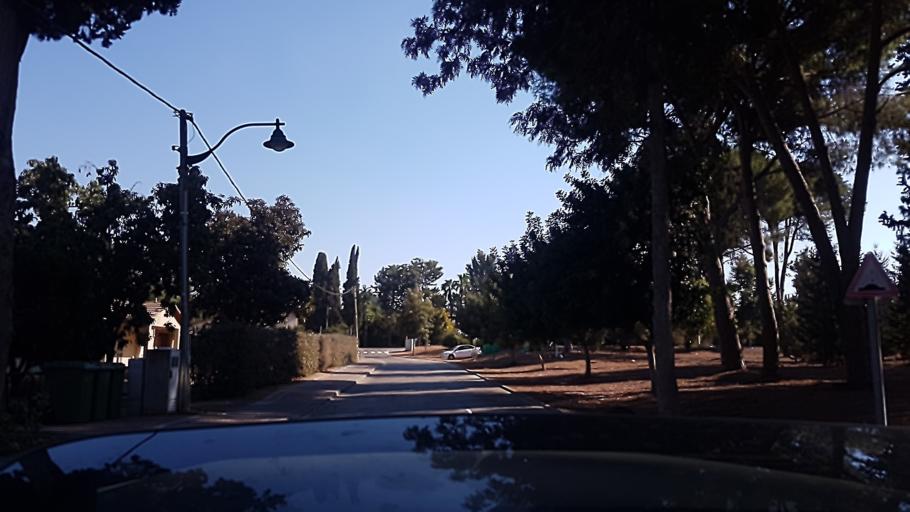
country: IL
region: Central District
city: Kfar Saba
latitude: 32.2108
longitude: 34.9011
